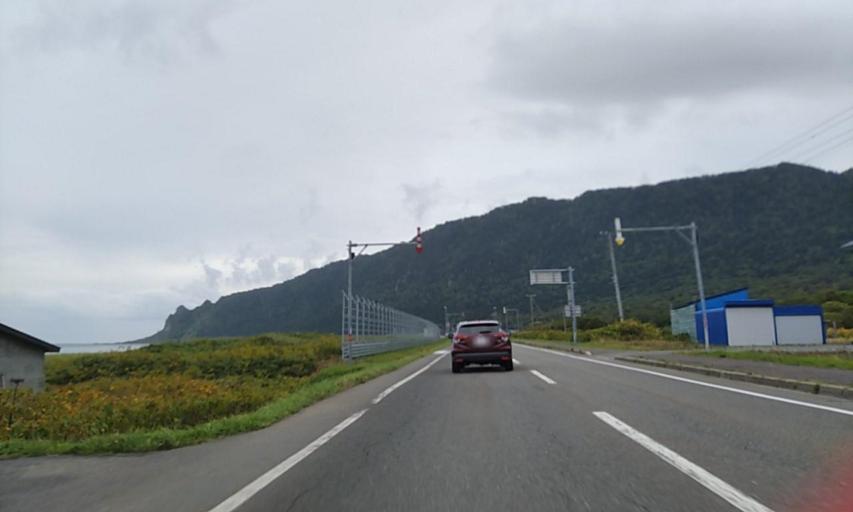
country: JP
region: Hokkaido
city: Nayoro
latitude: 45.0682
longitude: 142.4718
